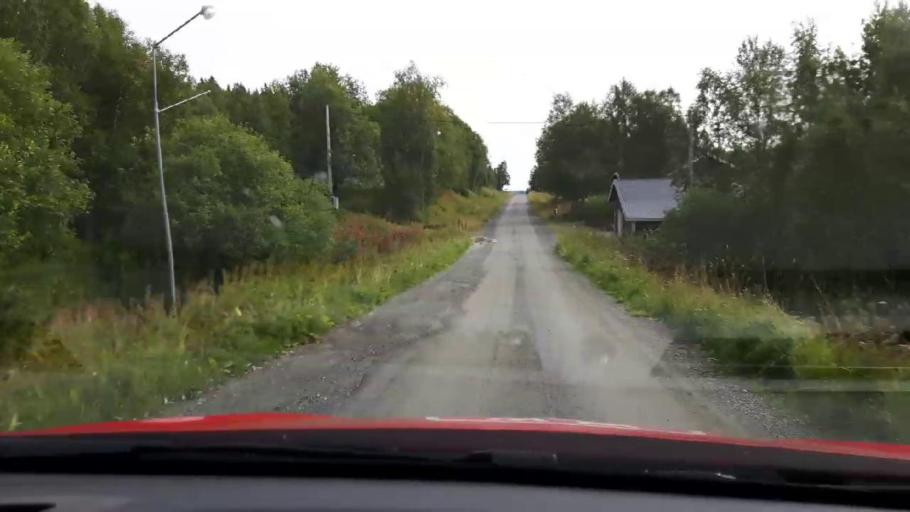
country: SE
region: Jaemtland
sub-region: Are Kommun
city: Are
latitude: 63.7497
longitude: 12.9611
